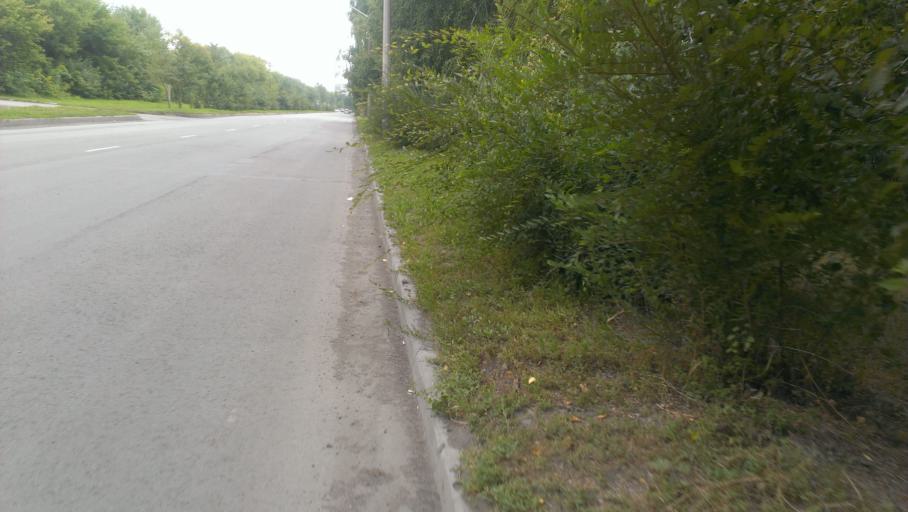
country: RU
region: Altai Krai
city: Yuzhnyy
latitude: 53.2534
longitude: 83.6985
